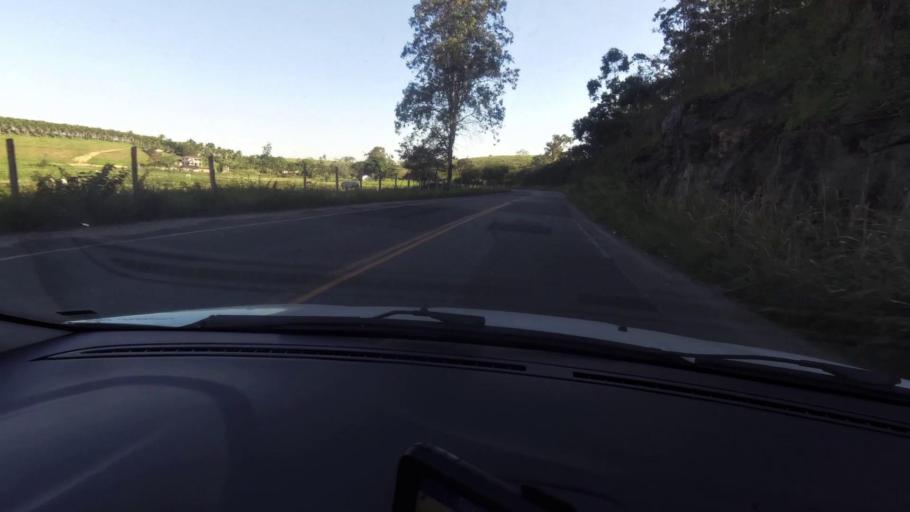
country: BR
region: Espirito Santo
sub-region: Piuma
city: Piuma
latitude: -20.7443
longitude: -40.6486
